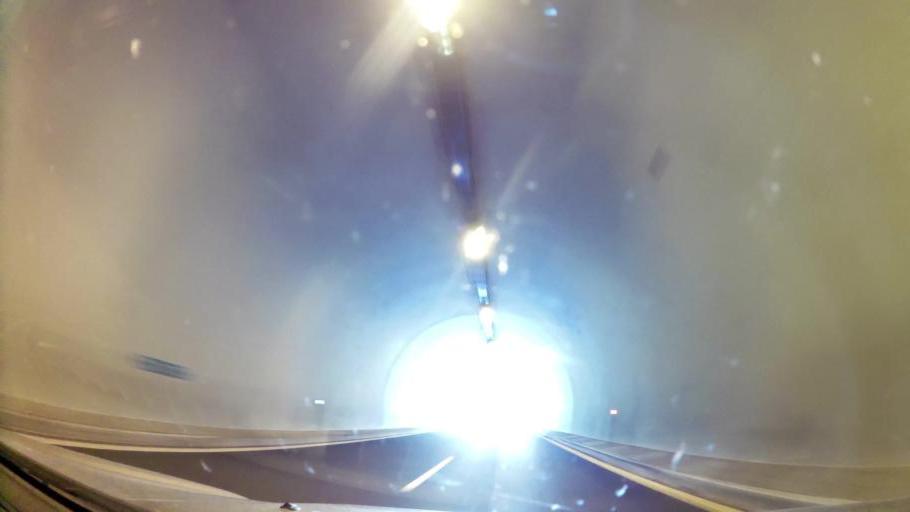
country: GR
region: Central Macedonia
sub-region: Nomos Imathias
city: Rizomata
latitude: 40.3813
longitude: 22.1085
